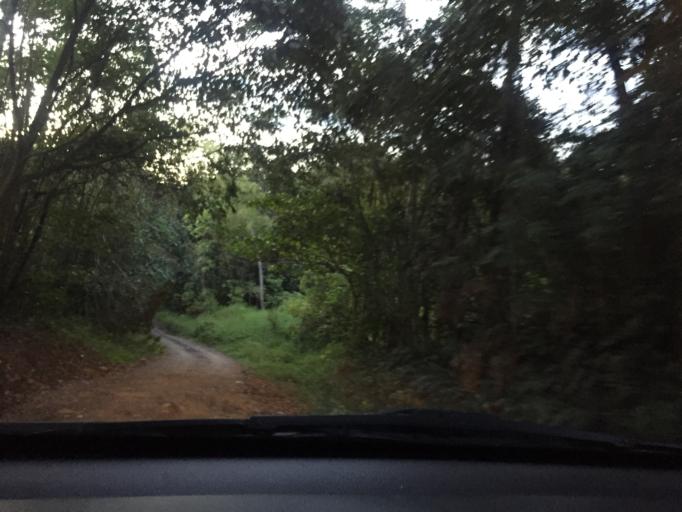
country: CO
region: Cundinamarca
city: Zipacon
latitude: 4.7106
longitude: -74.4094
